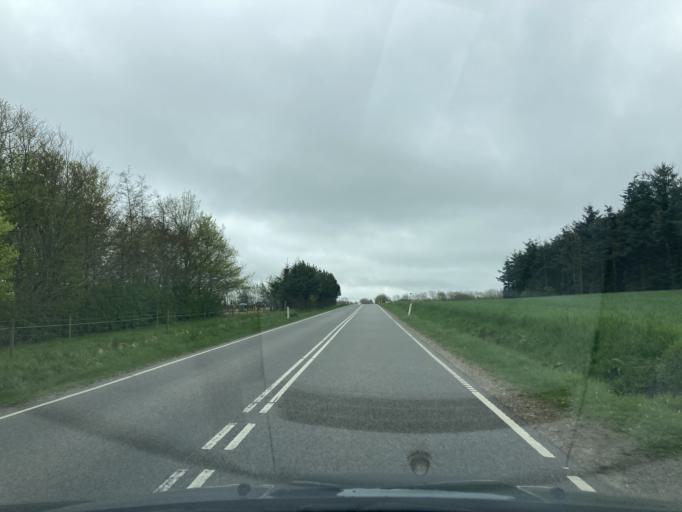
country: DK
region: North Denmark
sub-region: Thisted Kommune
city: Hurup
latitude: 56.8526
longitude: 8.3683
